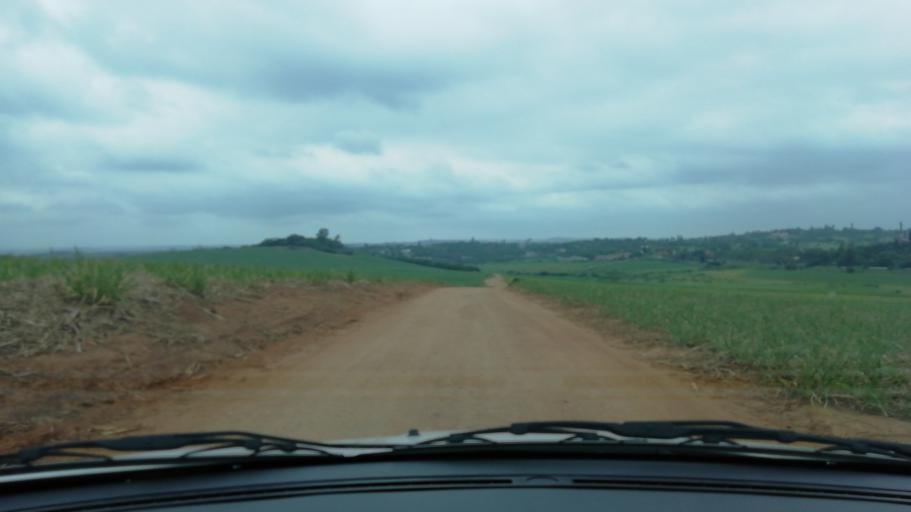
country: ZA
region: KwaZulu-Natal
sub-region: uThungulu District Municipality
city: Empangeni
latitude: -28.7311
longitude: 31.9080
